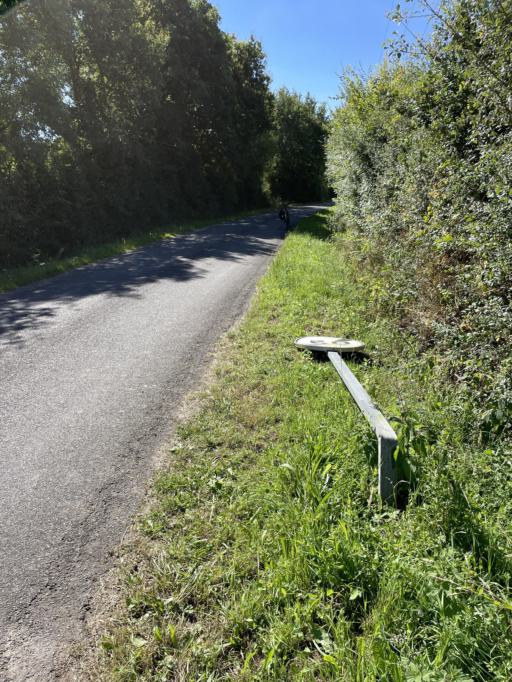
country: FR
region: Pays de la Loire
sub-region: Departement de la Loire-Atlantique
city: La Limouziniere
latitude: 46.9753
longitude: -1.6393
